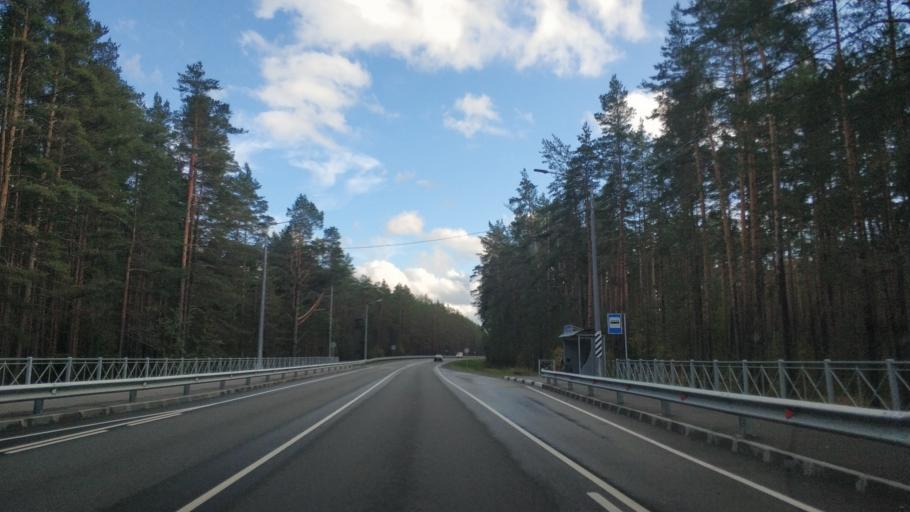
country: RU
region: Leningrad
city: Priozersk
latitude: 60.9941
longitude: 30.1827
